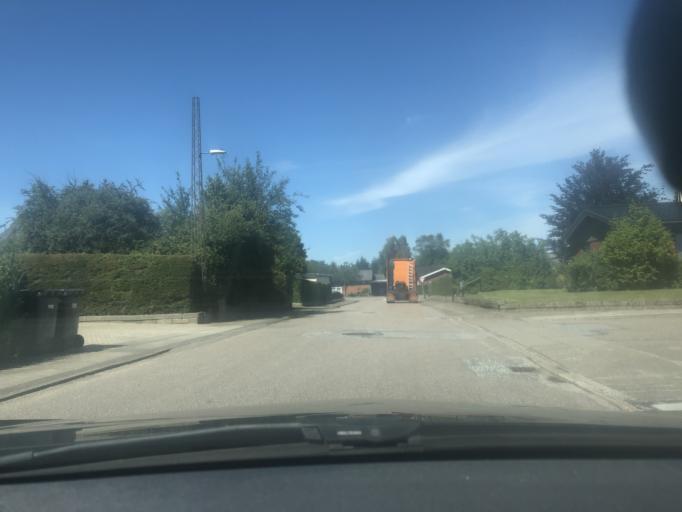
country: DK
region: South Denmark
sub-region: Vejle Kommune
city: Jelling
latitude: 55.6998
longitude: 9.3799
